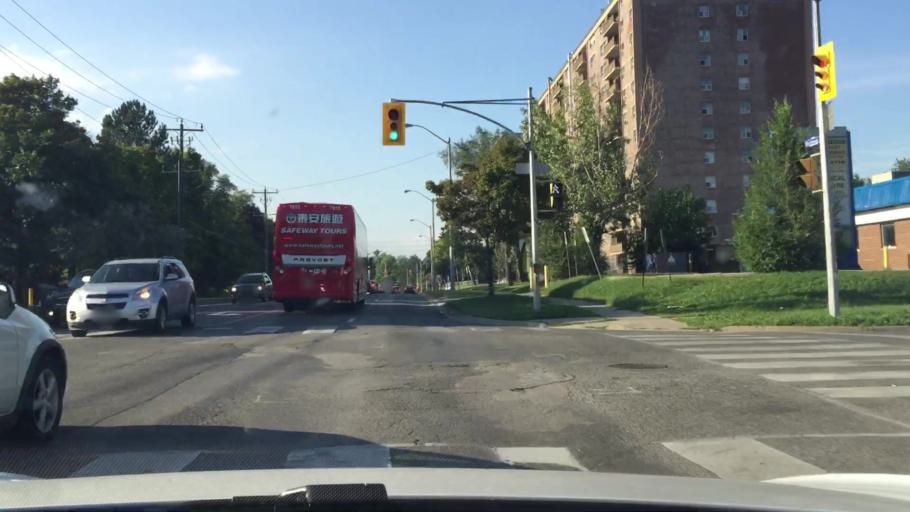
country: CA
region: Ontario
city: Scarborough
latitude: 43.7971
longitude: -79.3051
